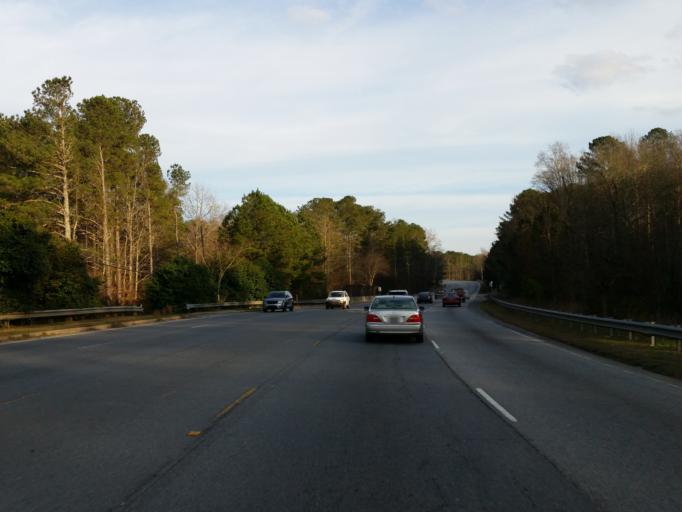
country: US
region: Georgia
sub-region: Cobb County
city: Powder Springs
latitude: 33.8597
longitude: -84.6542
